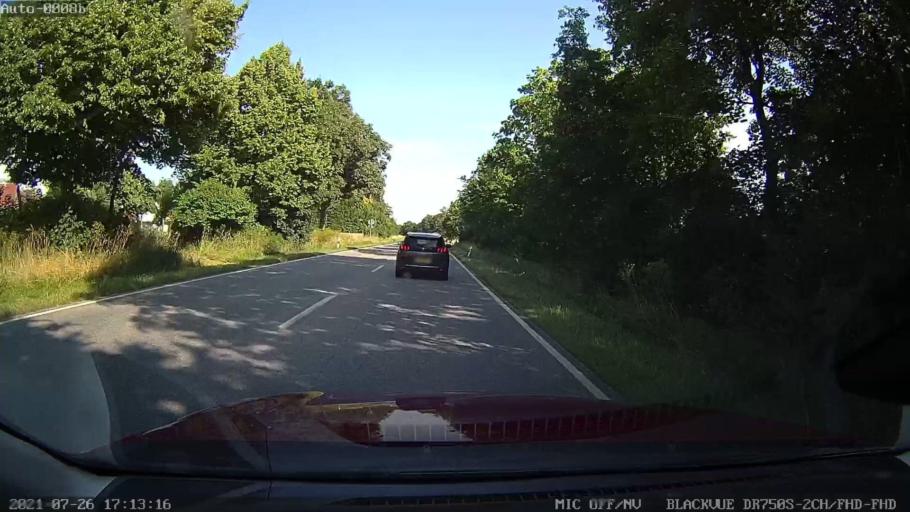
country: DE
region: Bavaria
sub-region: Upper Palatinate
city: Riekofen
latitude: 48.9712
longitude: 12.3153
